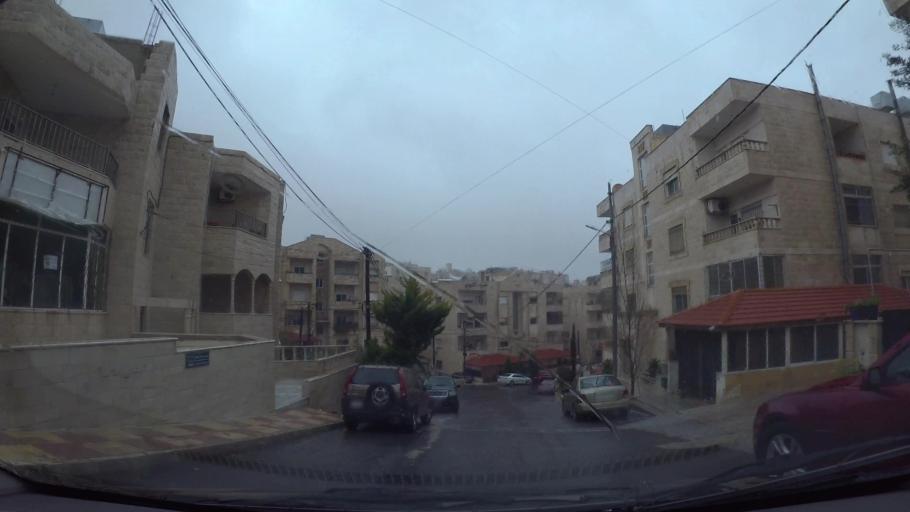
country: JO
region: Amman
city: Al Jubayhah
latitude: 32.0210
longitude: 35.8833
